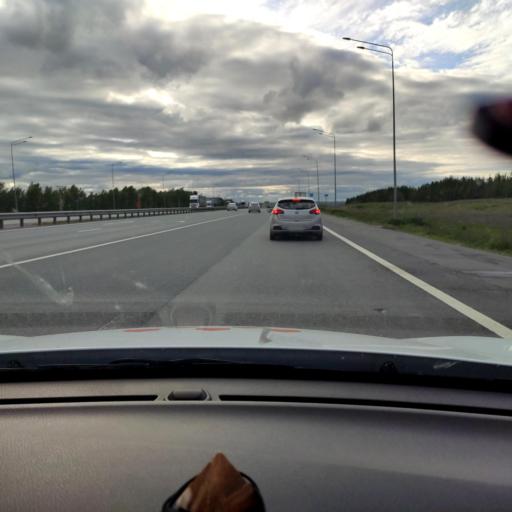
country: RU
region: Tatarstan
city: Pestretsy
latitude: 55.6774
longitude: 49.6951
